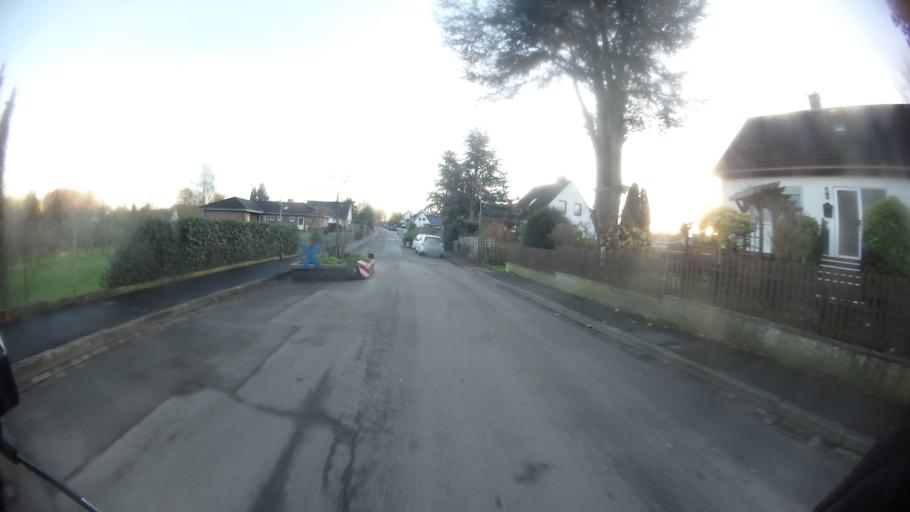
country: DE
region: Schleswig-Holstein
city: Scharbeutz
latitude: 54.0211
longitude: 10.7070
